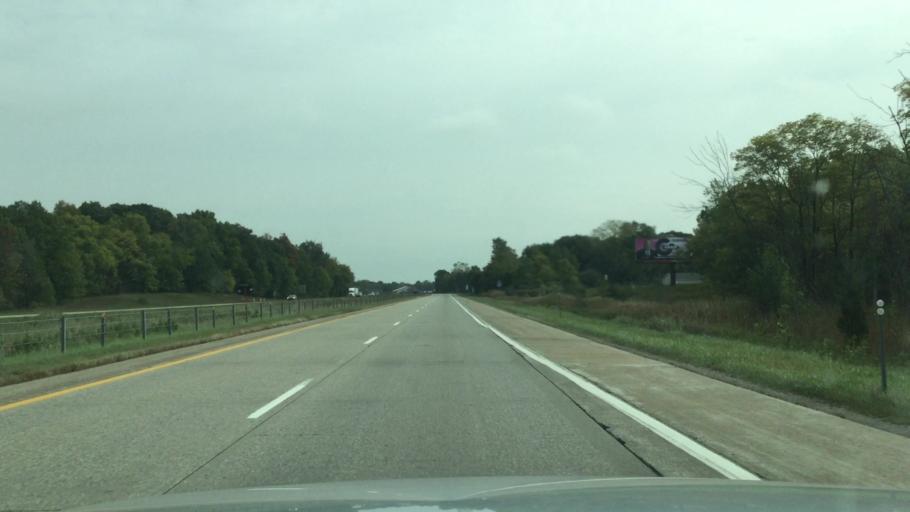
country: US
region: Michigan
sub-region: Shiawassee County
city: Perry
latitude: 42.8406
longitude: -84.2099
